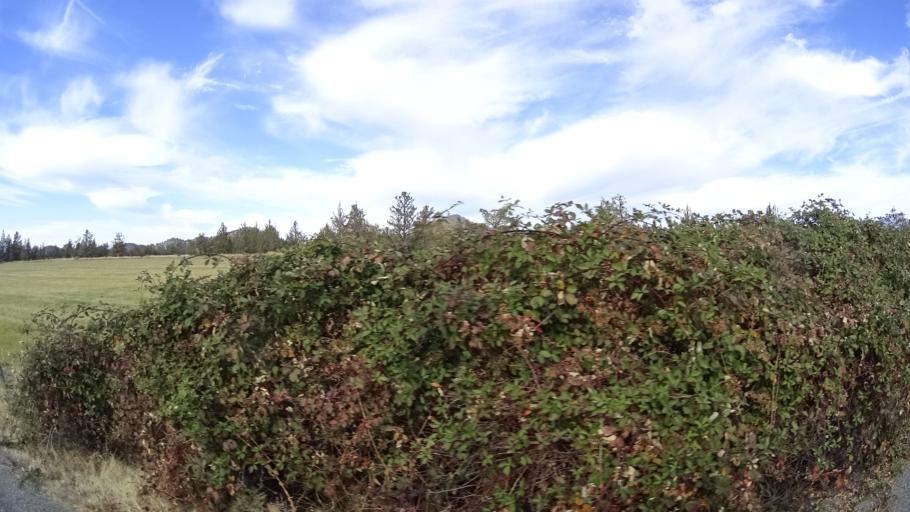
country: US
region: California
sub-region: Siskiyou County
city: Montague
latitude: 41.6384
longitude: -122.4259
